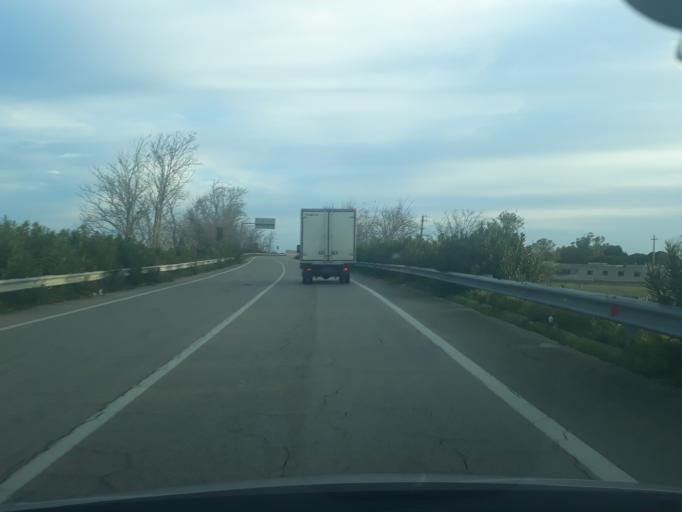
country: IT
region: Apulia
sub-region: Provincia di Brindisi
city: Brindisi
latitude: 40.6566
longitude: 17.9068
